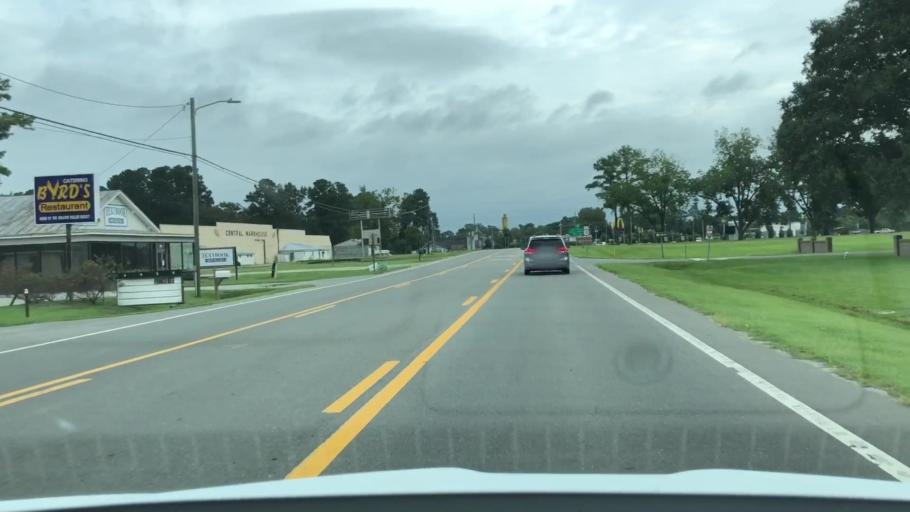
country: US
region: North Carolina
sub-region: Lenoir County
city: Kinston
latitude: 35.2345
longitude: -77.5741
